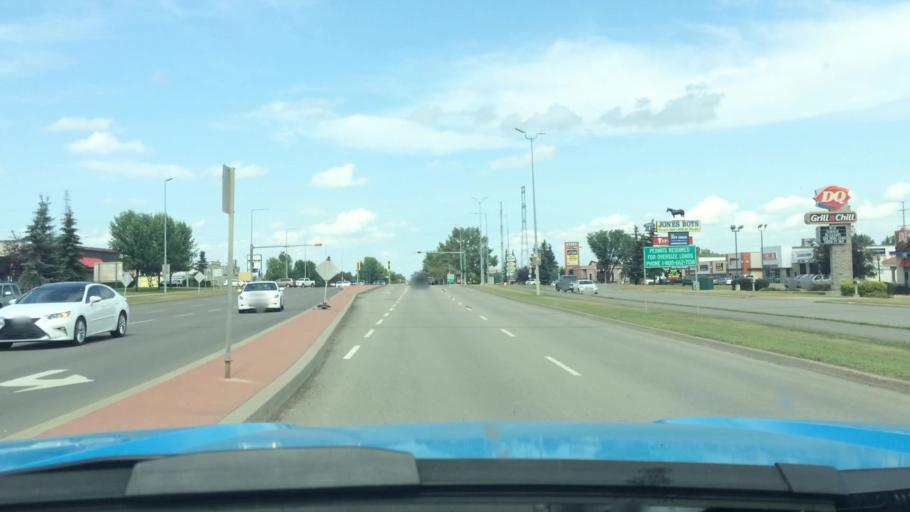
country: CA
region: Alberta
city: Red Deer
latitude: 52.2340
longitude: -113.8139
